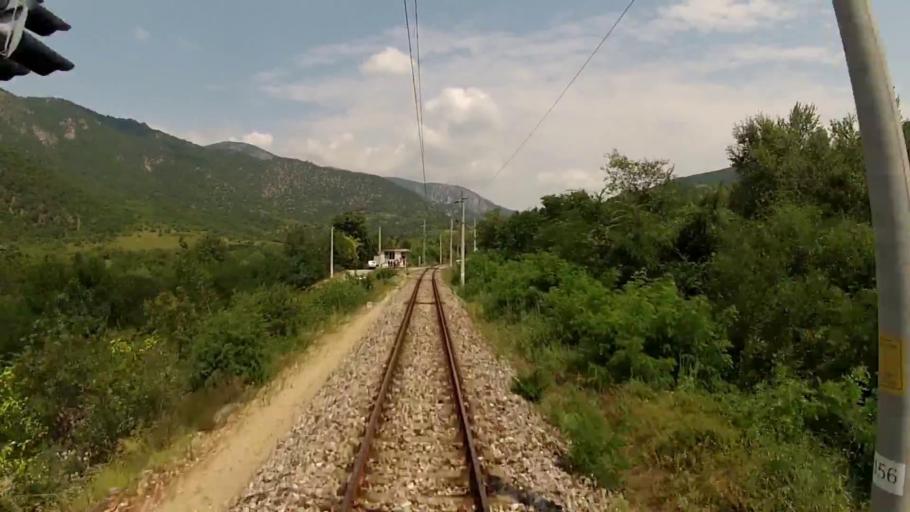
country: BG
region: Blagoevgrad
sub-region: Obshtina Kresna
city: Kresna
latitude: 41.7487
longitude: 23.1571
